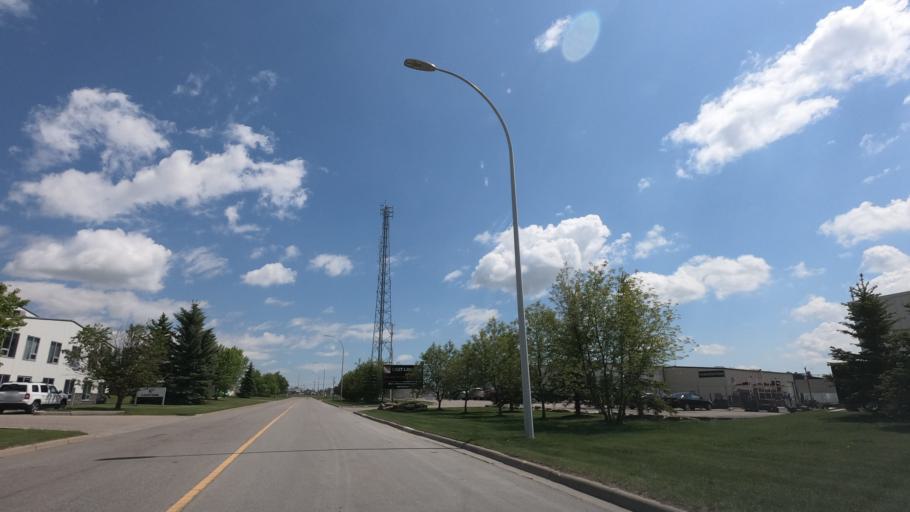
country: CA
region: Alberta
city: Airdrie
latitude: 51.2935
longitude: -113.9940
